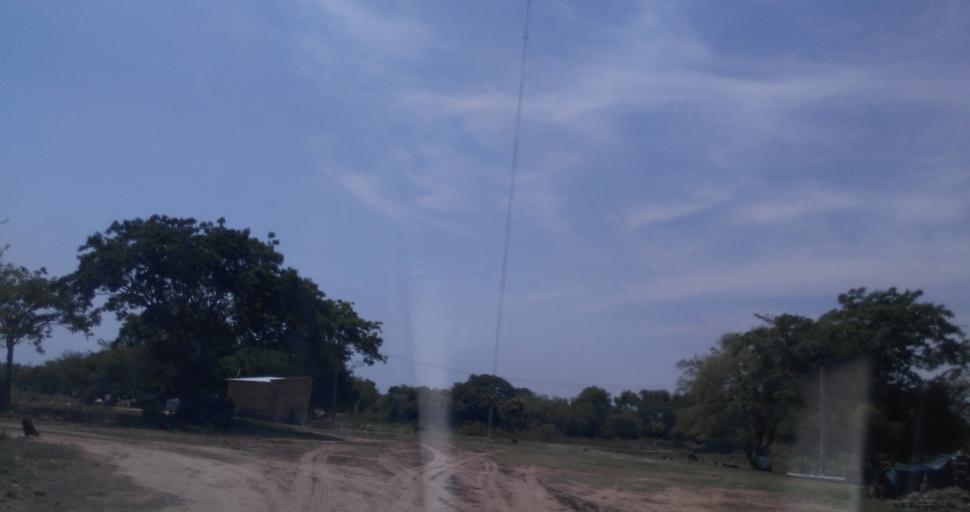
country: AR
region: Chaco
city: Fontana
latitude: -27.4170
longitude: -59.0125
